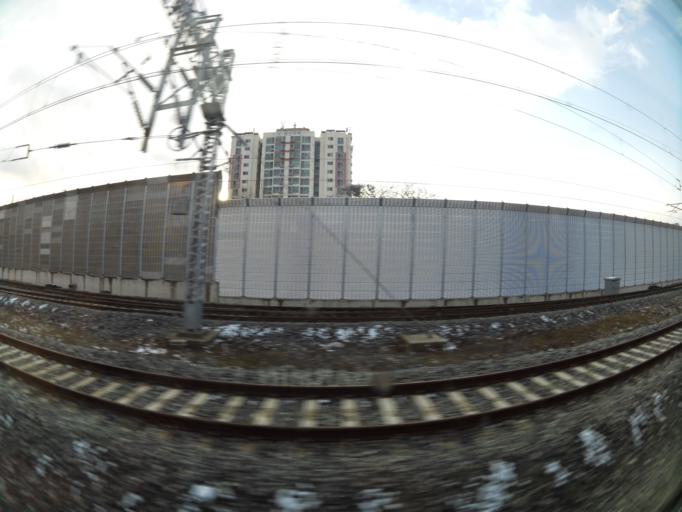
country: KR
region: Daejeon
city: Daejeon
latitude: 36.3374
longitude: 127.4315
